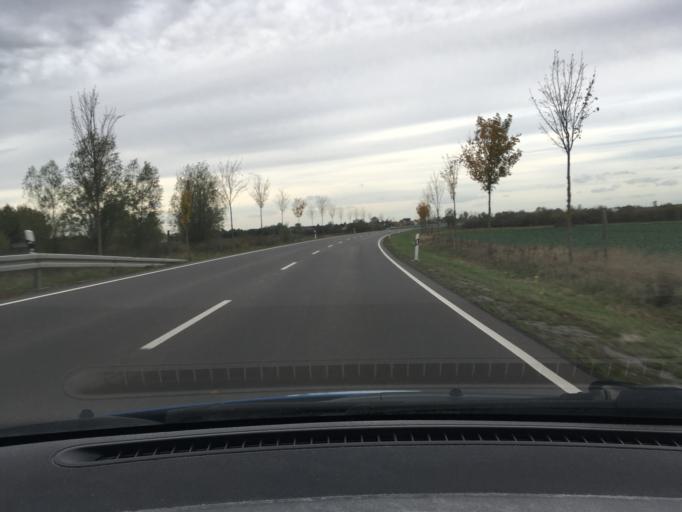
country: DE
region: Saxony-Anhalt
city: Leitzkau
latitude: 52.0671
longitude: 11.8888
